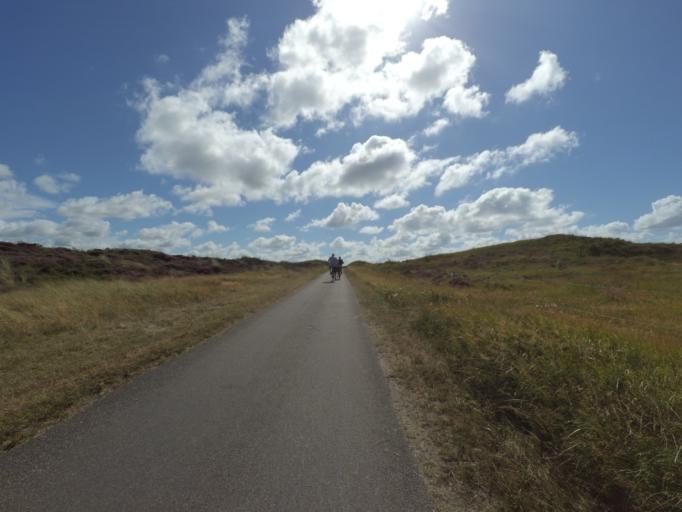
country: NL
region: North Holland
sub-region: Gemeente Texel
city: Den Burg
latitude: 53.1107
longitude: 4.7930
